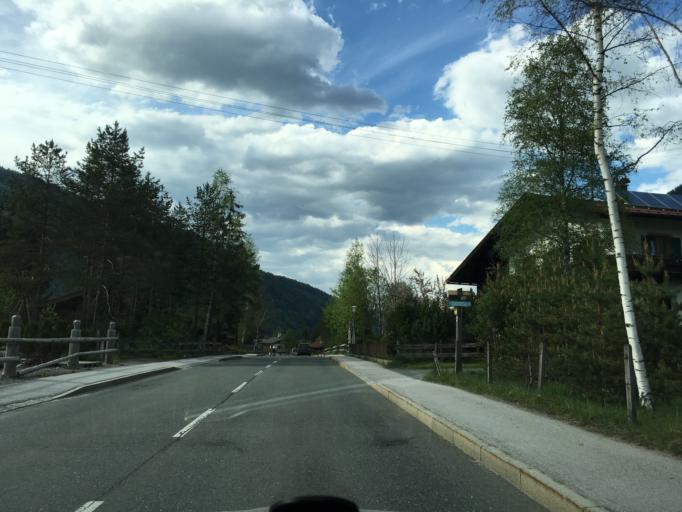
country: AT
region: Tyrol
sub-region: Politischer Bezirk Kitzbuhel
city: Fieberbrunn
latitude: 47.5230
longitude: 12.5777
